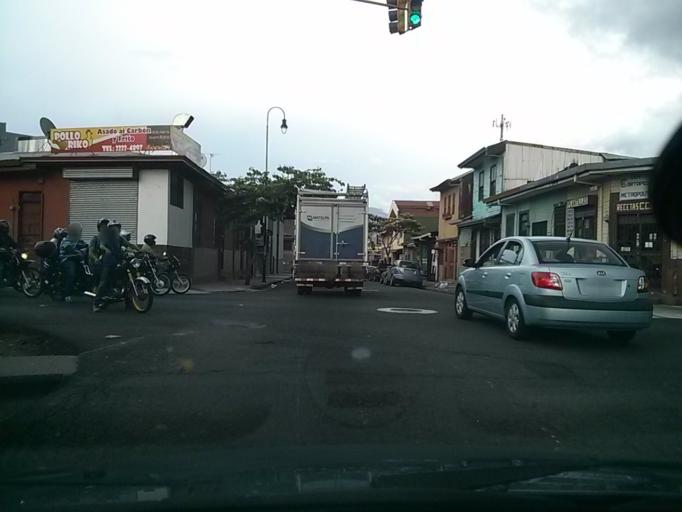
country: CR
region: San Jose
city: San Jose
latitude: 9.9281
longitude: -84.0837
